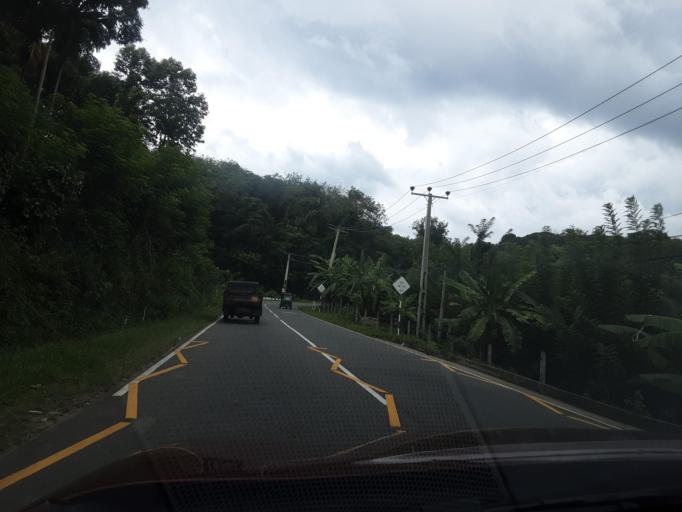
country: LK
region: Uva
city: Monaragala
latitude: 6.9012
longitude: 81.2141
